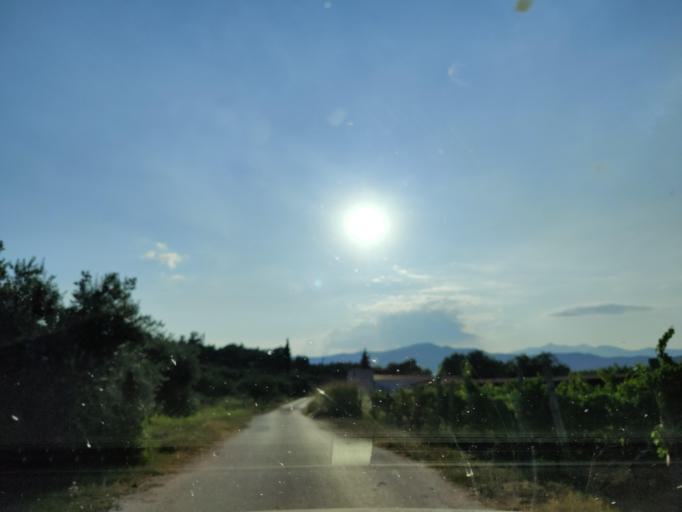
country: GR
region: East Macedonia and Thrace
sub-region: Nomos Kavalas
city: Nea Peramos
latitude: 40.8298
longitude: 24.2988
